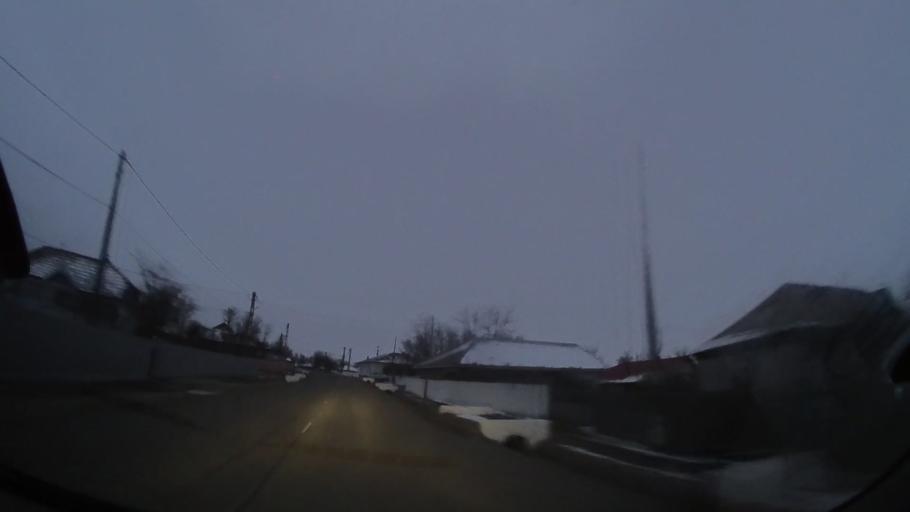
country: RO
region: Vaslui
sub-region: Comuna Vutcani
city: Vutcani
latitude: 46.4561
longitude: 28.0237
